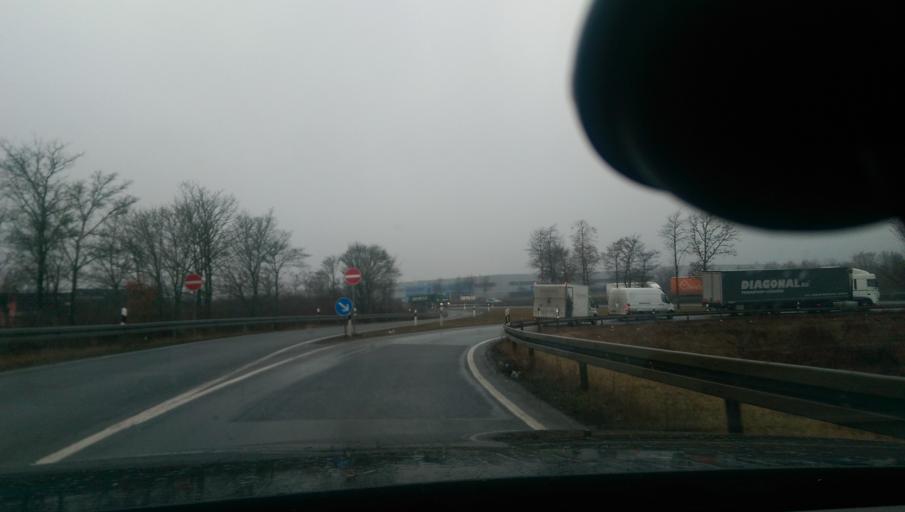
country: DE
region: Lower Saxony
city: Sehnde
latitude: 52.3576
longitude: 9.8863
